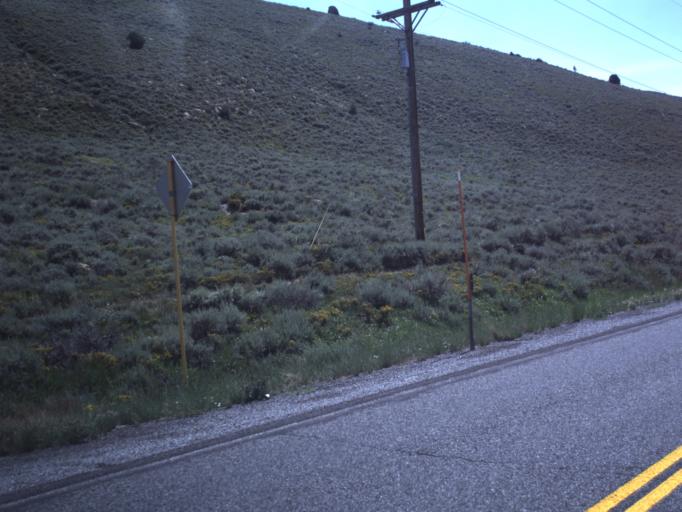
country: US
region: Utah
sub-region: Carbon County
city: Helper
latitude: 39.7995
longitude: -111.1334
